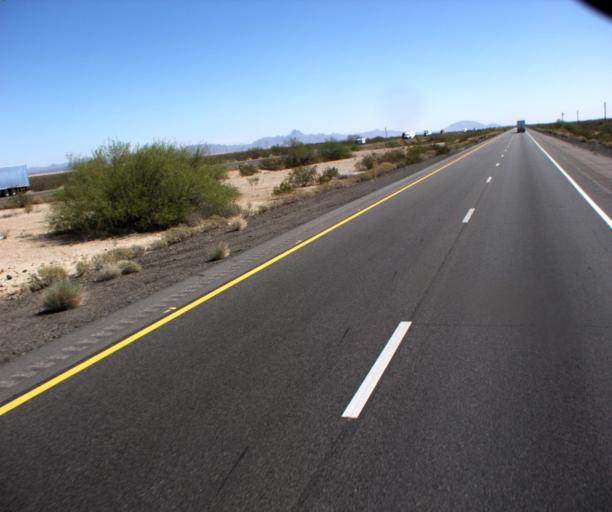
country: US
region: Arizona
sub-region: La Paz County
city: Salome
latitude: 33.5746
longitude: -113.3919
